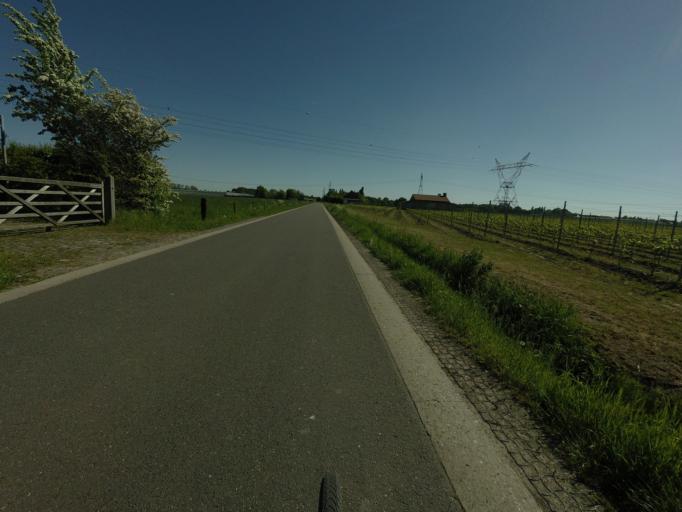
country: BE
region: Flanders
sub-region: Provincie Antwerpen
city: Boechout
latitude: 51.1768
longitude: 4.4998
